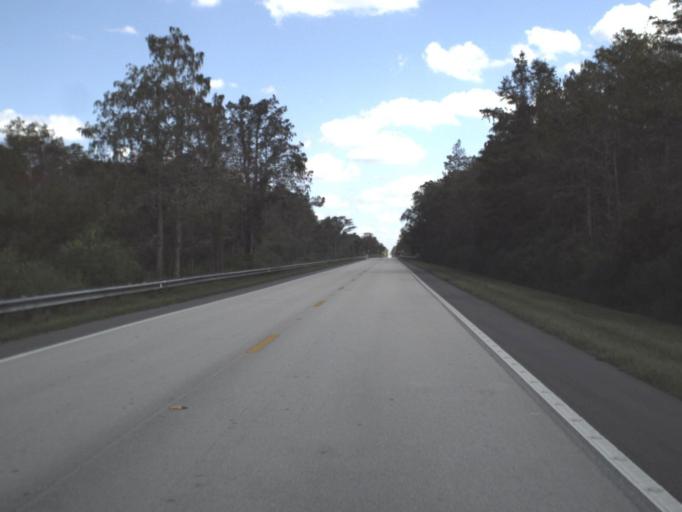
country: US
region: Florida
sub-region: Miami-Dade County
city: Kendall West
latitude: 25.8582
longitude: -81.0469
